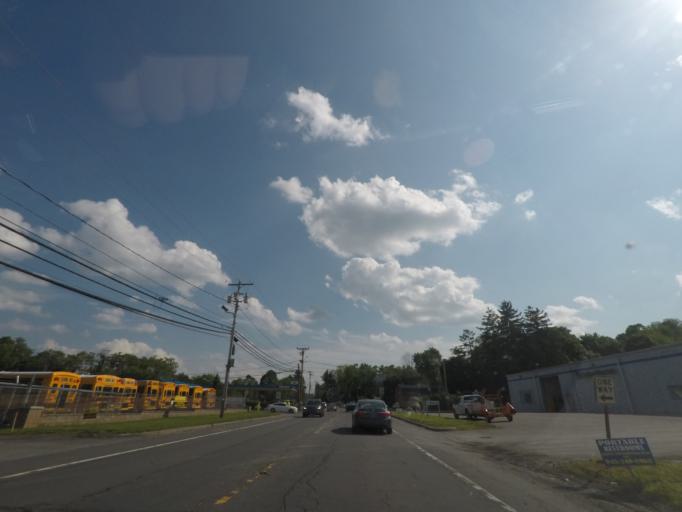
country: US
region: New York
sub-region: Orange County
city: Balmville
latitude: 41.5563
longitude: -74.0045
